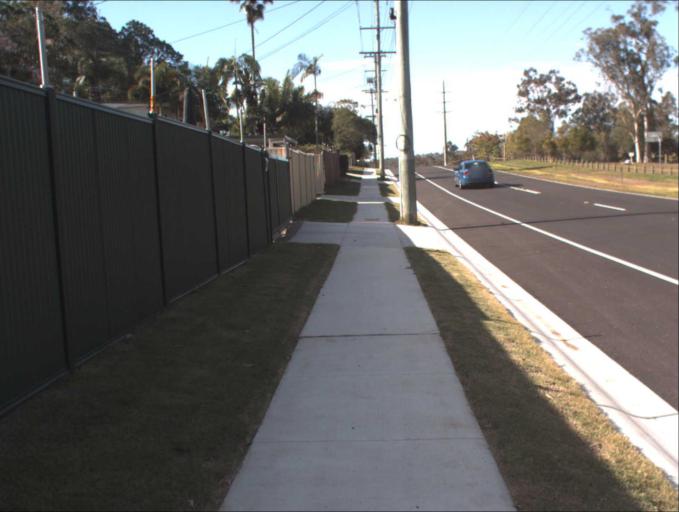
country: AU
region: Queensland
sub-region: Logan
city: Slacks Creek
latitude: -27.6508
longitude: 153.1354
